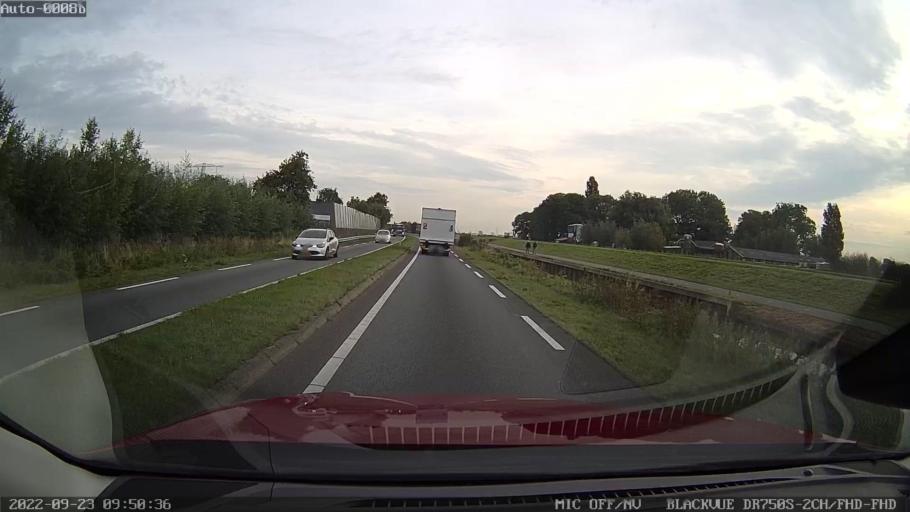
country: NL
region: South Holland
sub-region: Gemeente Westland
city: Kwintsheul
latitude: 51.9983
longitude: 4.2699
